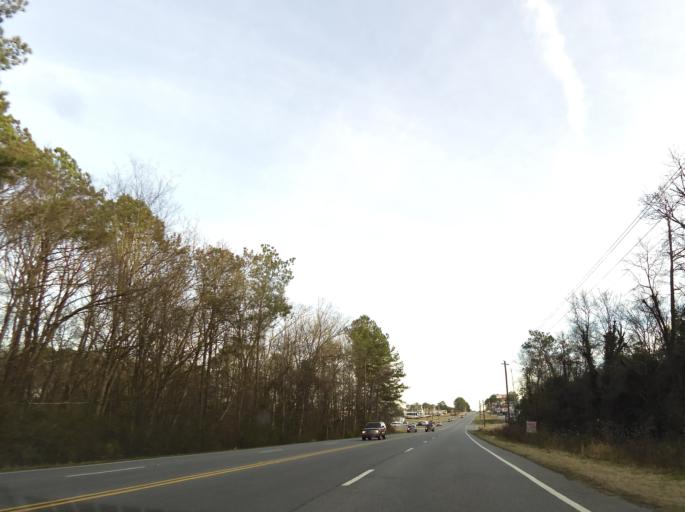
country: US
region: Georgia
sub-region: Bibb County
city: Macon
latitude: 32.8611
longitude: -83.6495
